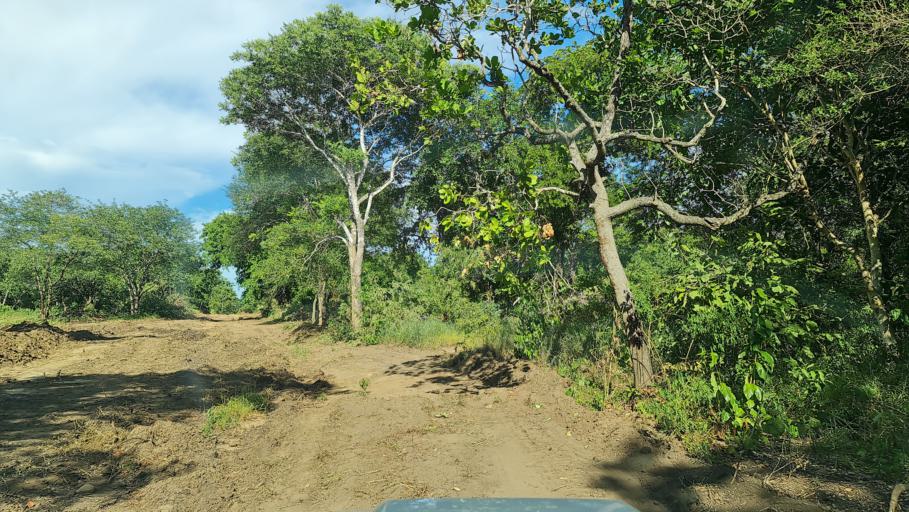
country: MZ
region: Nampula
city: Ilha de Mocambique
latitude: -15.5077
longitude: 40.1436
